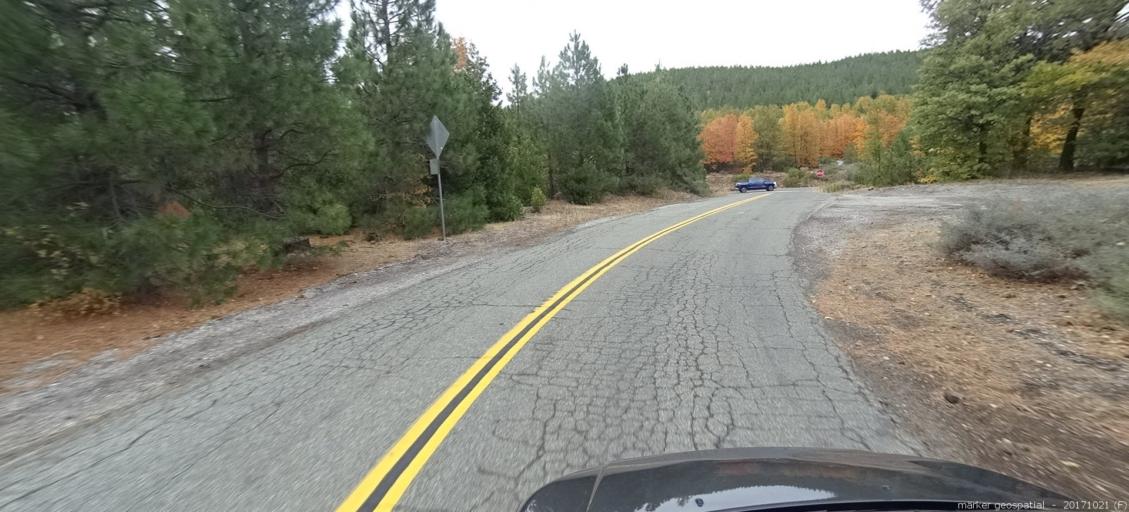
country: US
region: California
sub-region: Shasta County
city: Burney
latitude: 40.8652
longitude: -121.8494
